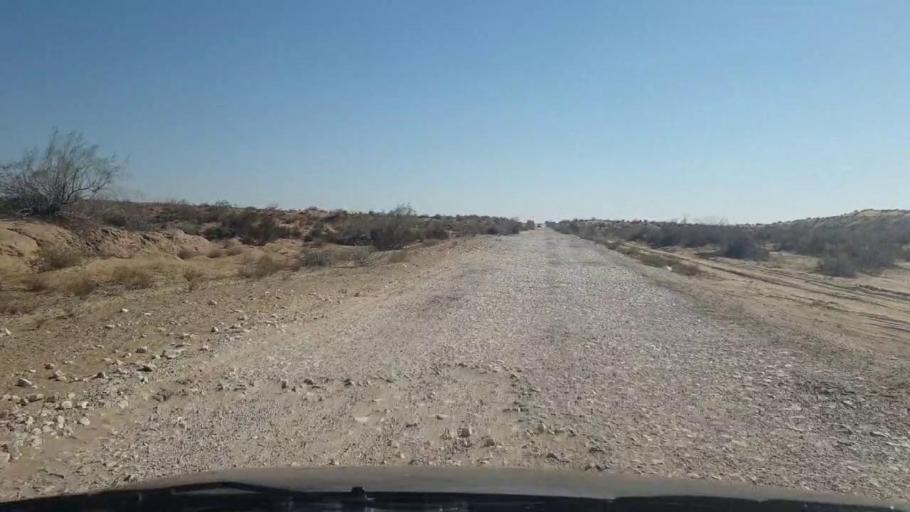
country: PK
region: Sindh
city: Bozdar
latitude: 27.0282
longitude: 68.7079
